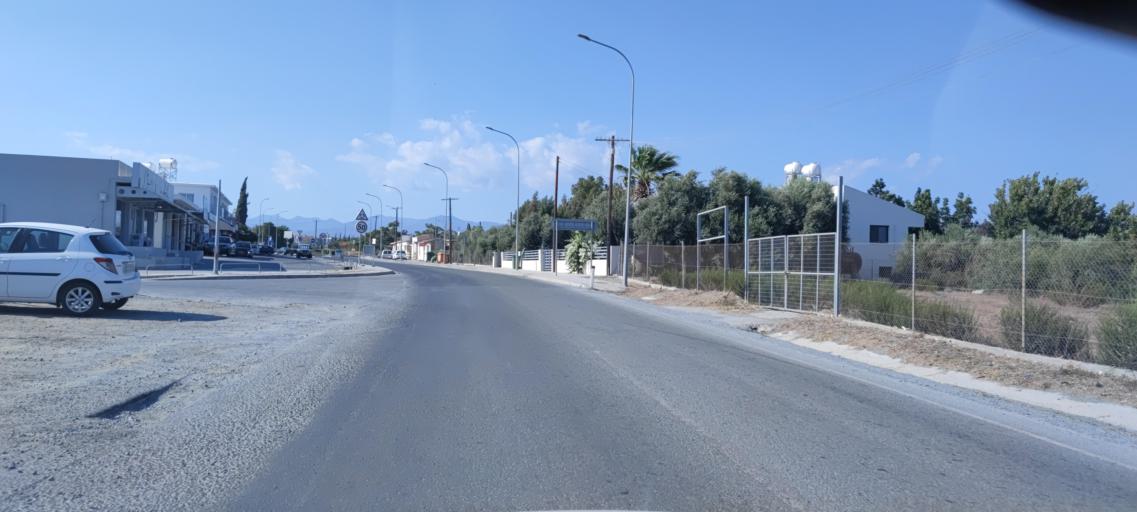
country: CY
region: Larnaka
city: Kofinou
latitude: 34.7508
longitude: 33.3160
